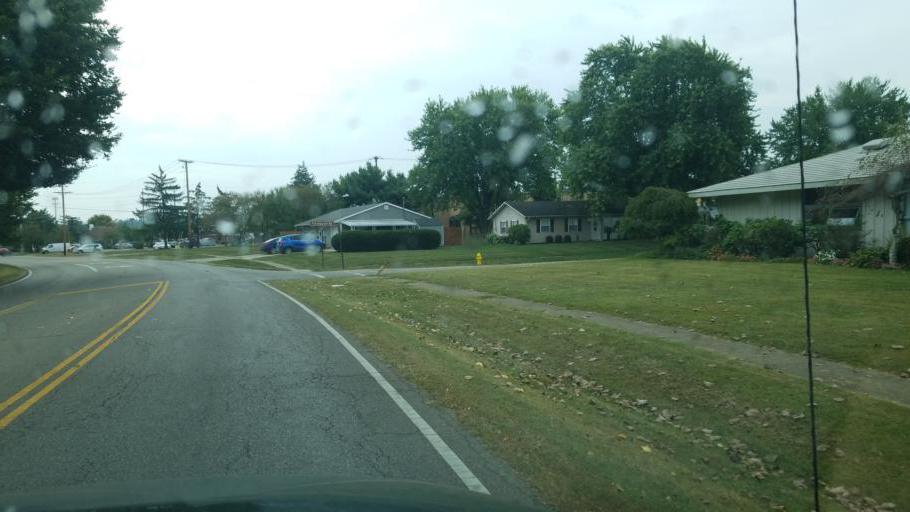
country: US
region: Ohio
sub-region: Licking County
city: Heath
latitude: 40.0390
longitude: -82.4324
